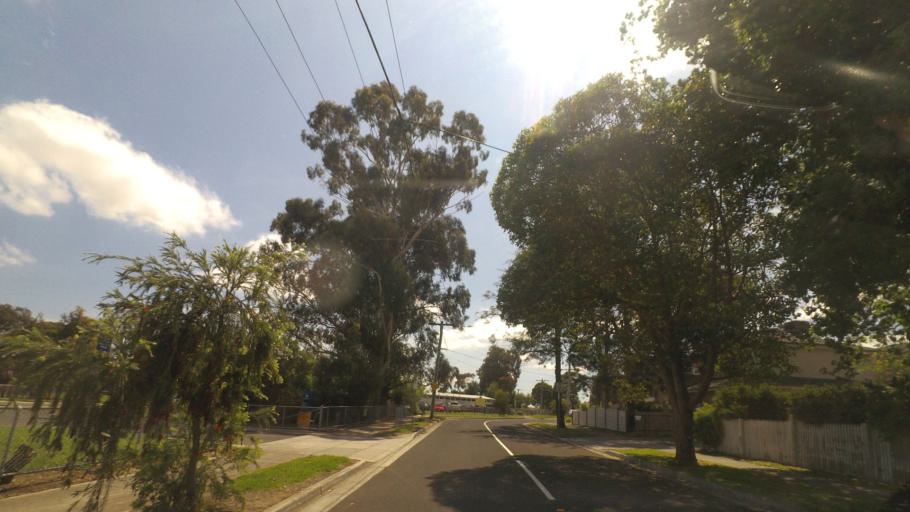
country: AU
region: Victoria
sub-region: Knox
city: Bayswater
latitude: -37.8441
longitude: 145.2593
